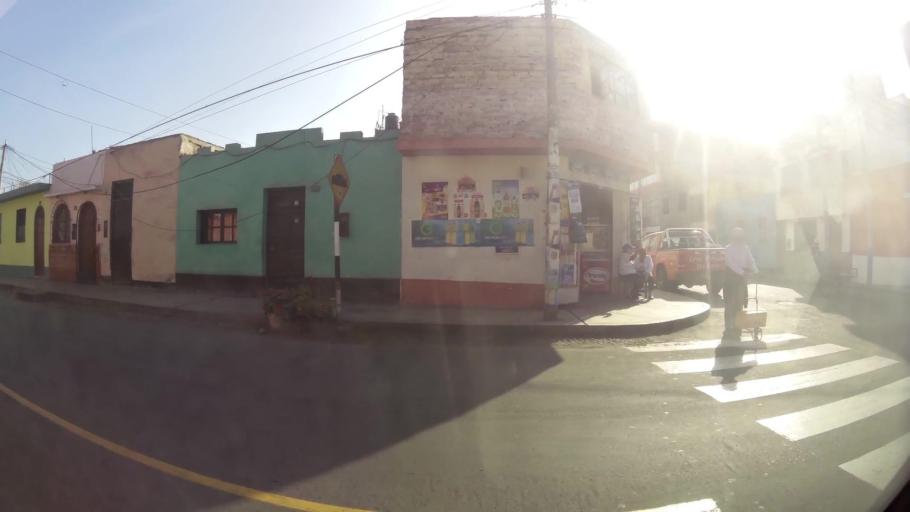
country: PE
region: Lima
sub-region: Huaura
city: Huacho
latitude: -11.1101
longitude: -77.6121
